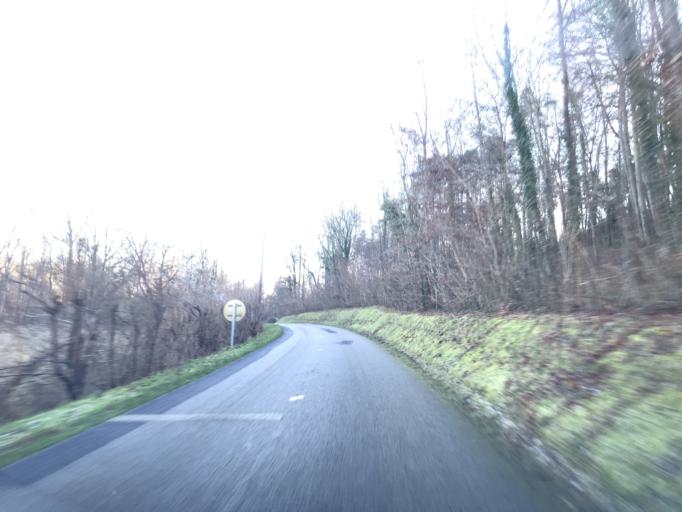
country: FR
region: Haute-Normandie
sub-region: Departement de l'Eure
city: Heudreville-sur-Eure
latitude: 49.0916
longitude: 1.2603
